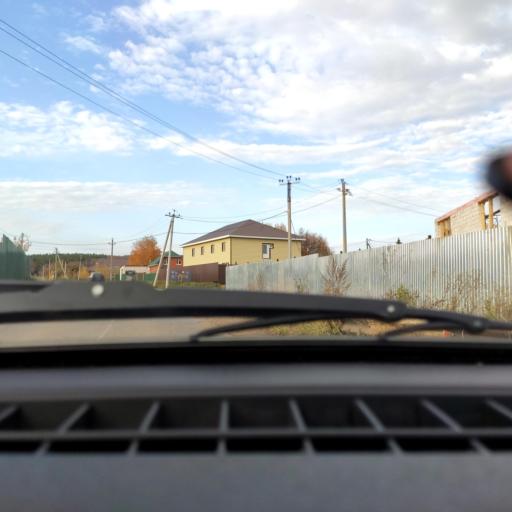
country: RU
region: Bashkortostan
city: Mikhaylovka
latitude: 54.8021
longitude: 55.8804
